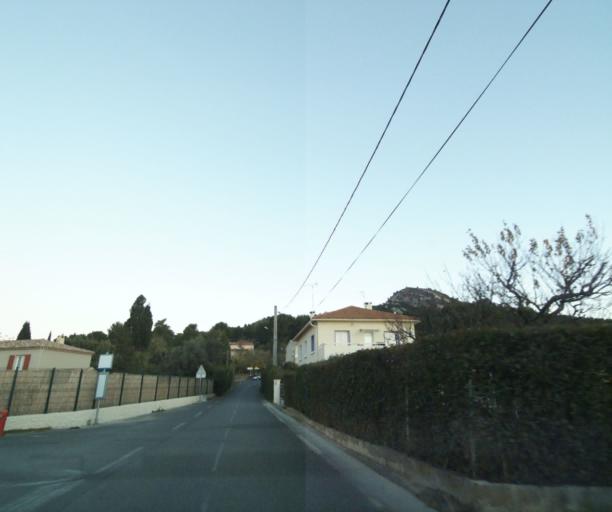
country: FR
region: Provence-Alpes-Cote d'Azur
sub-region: Departement des Bouches-du-Rhone
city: La Penne-sur-Huveaune
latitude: 43.3023
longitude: 5.5298
